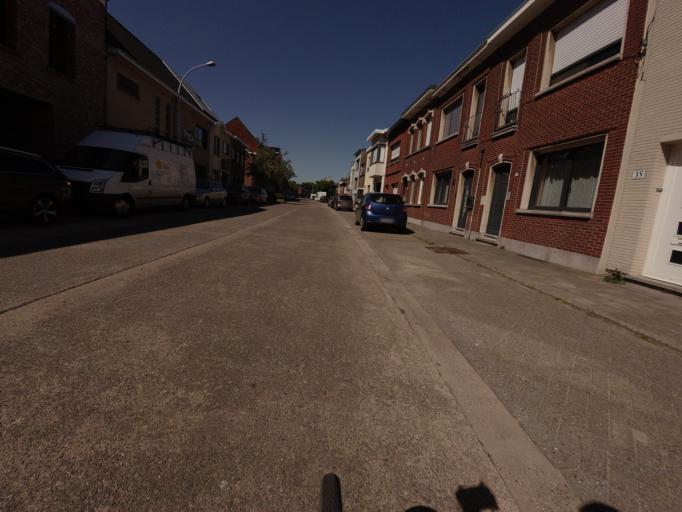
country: BE
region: Flanders
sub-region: Provincie Antwerpen
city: Borsbeek
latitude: 51.1940
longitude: 4.4907
